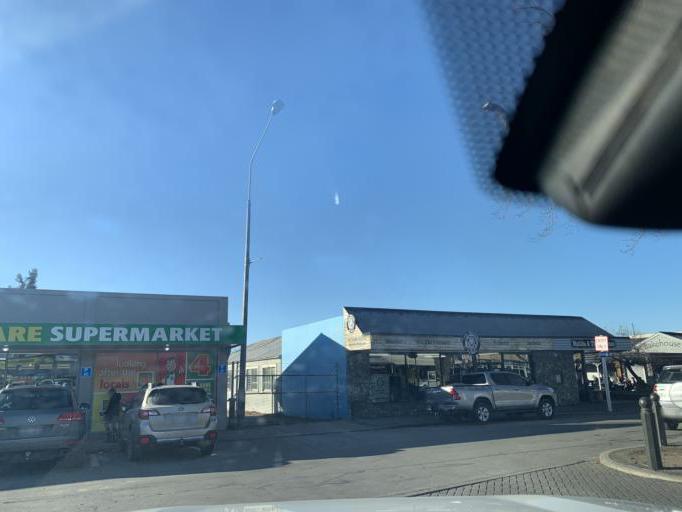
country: NZ
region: Canterbury
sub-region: Timaru District
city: Pleasant Point
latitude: -44.0982
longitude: 170.8291
